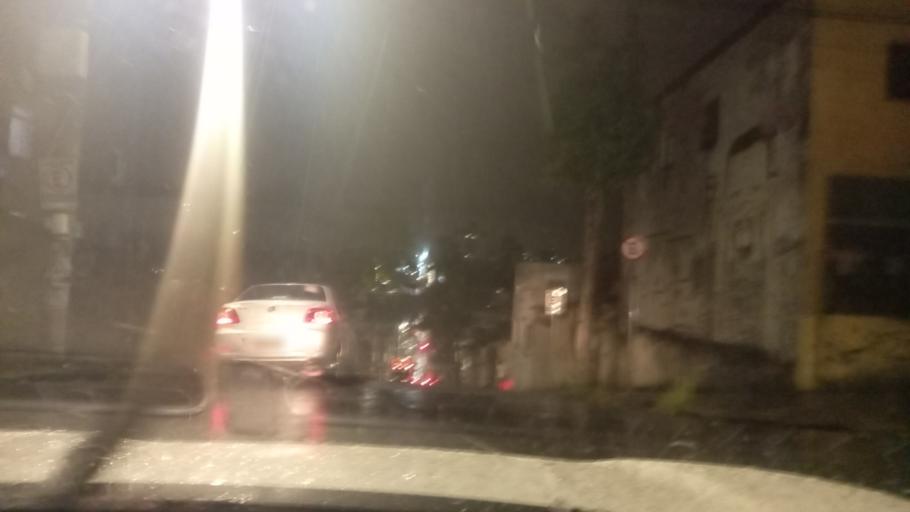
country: BR
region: Minas Gerais
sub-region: Belo Horizonte
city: Belo Horizonte
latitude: -19.9138
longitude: -43.9765
